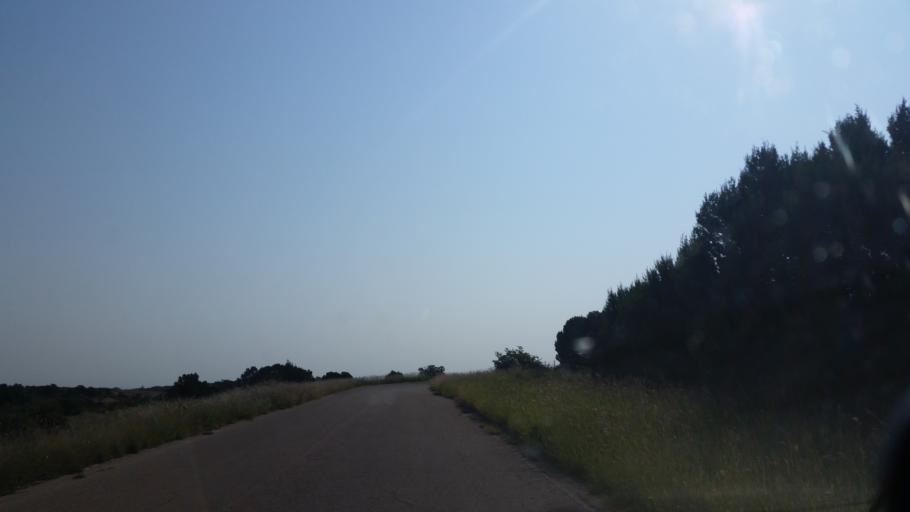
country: US
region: New Mexico
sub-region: Quay County
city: Logan
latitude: 34.9846
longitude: -103.3591
